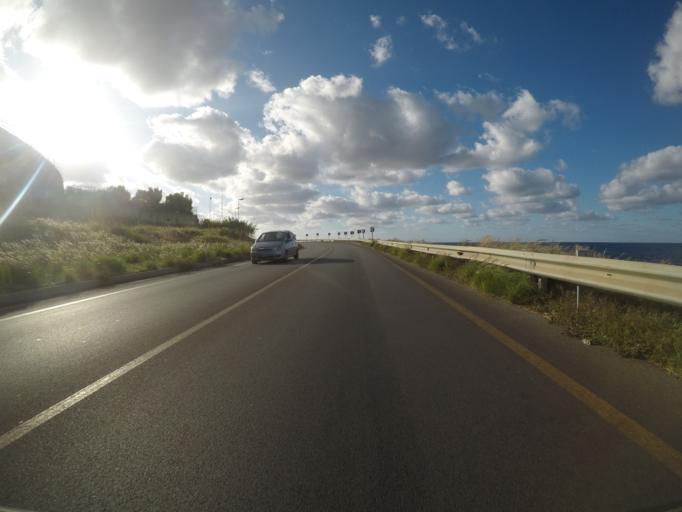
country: IT
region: Sicily
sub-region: Palermo
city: Isola delle Femmine
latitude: 38.2001
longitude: 13.2591
